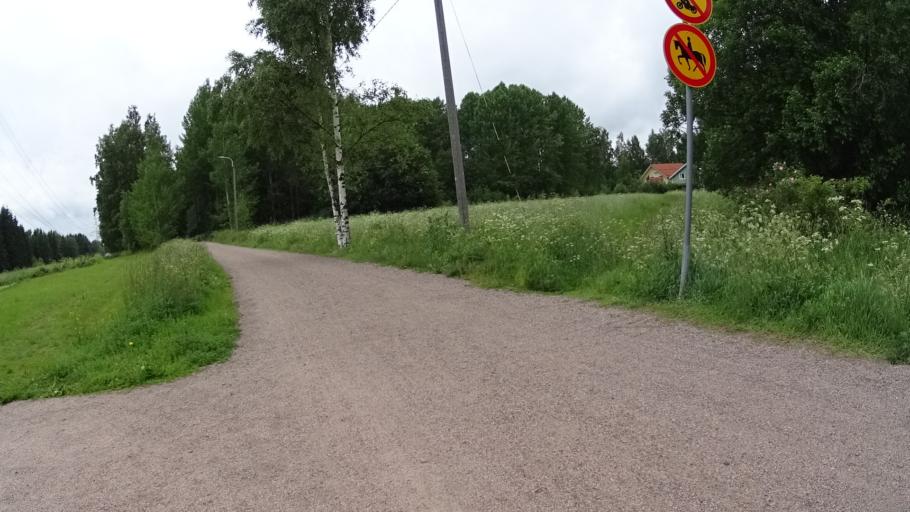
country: FI
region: Uusimaa
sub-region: Helsinki
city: Helsinki
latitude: 60.2731
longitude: 24.9107
